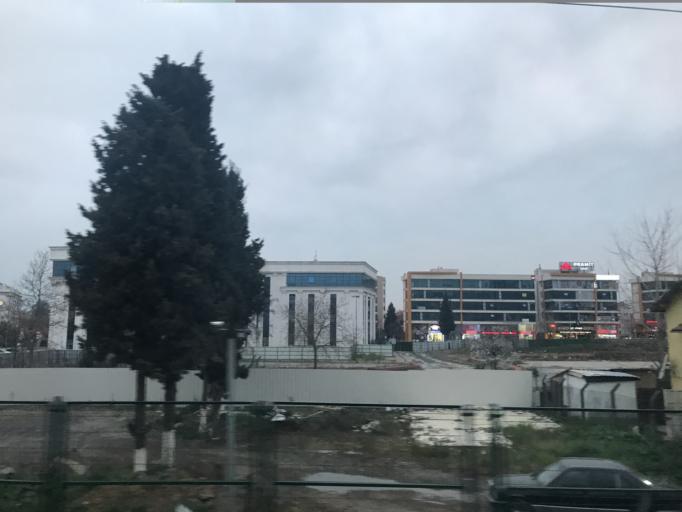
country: TR
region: Istanbul
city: Icmeler
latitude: 40.8445
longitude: 29.3012
